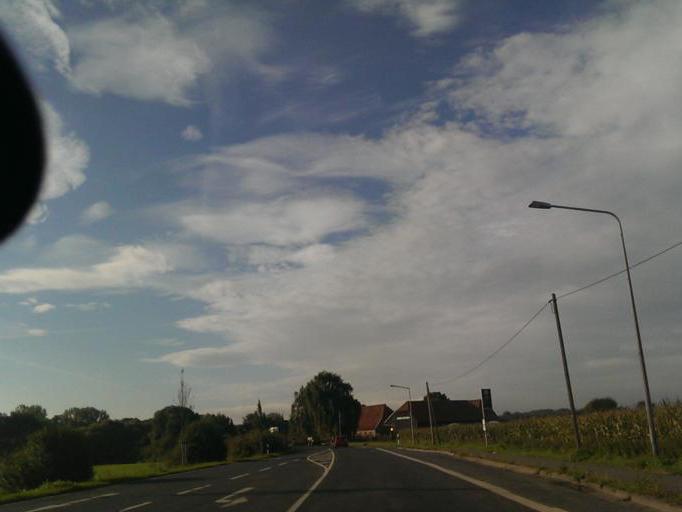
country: DE
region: Lower Saxony
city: Wunstorf
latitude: 52.4390
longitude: 9.4485
